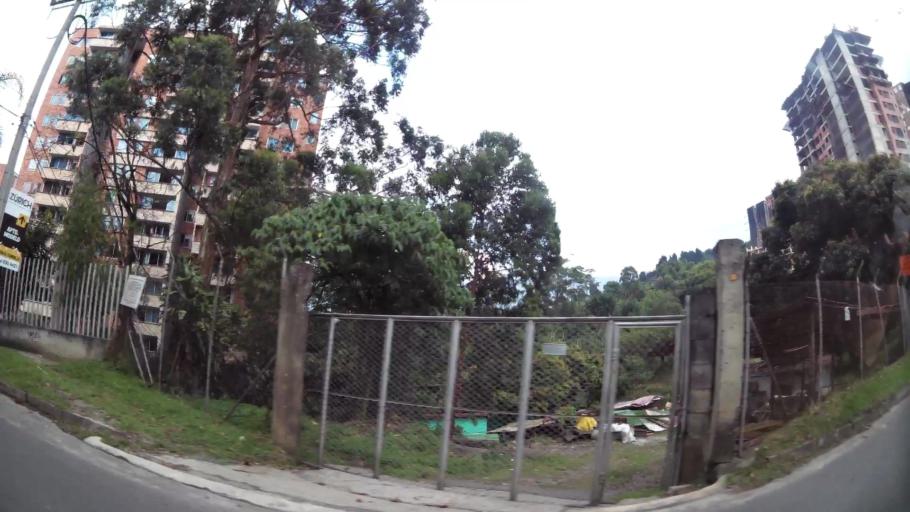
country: CO
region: Antioquia
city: Sabaneta
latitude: 6.1570
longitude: -75.5981
